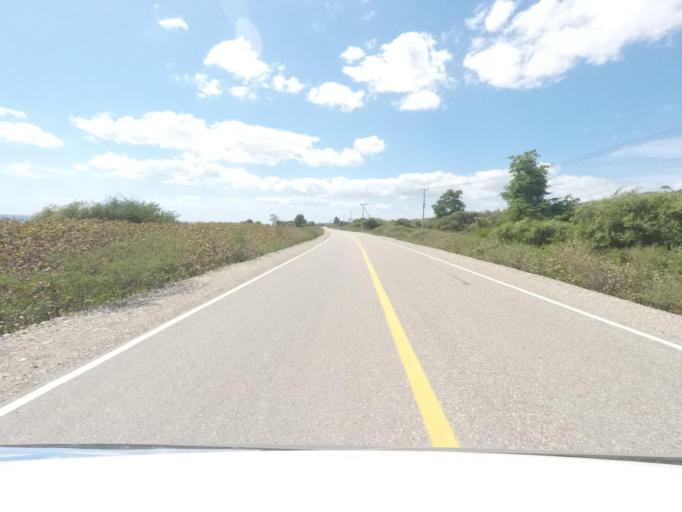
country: TL
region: Baucau
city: Baucau
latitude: -8.4588
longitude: 126.6135
